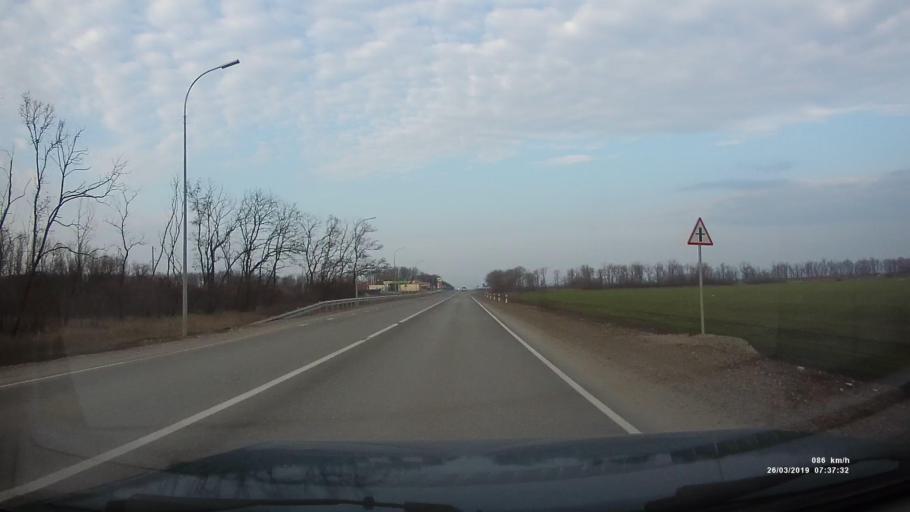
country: RU
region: Rostov
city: Novobessergenovka
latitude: 47.2022
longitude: 38.6998
